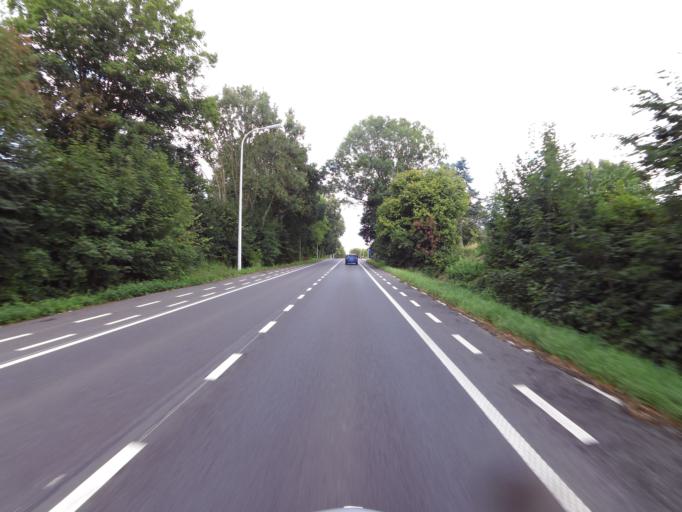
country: BE
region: Wallonia
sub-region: Province du Hainaut
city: Mons
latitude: 50.4417
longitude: 3.9875
